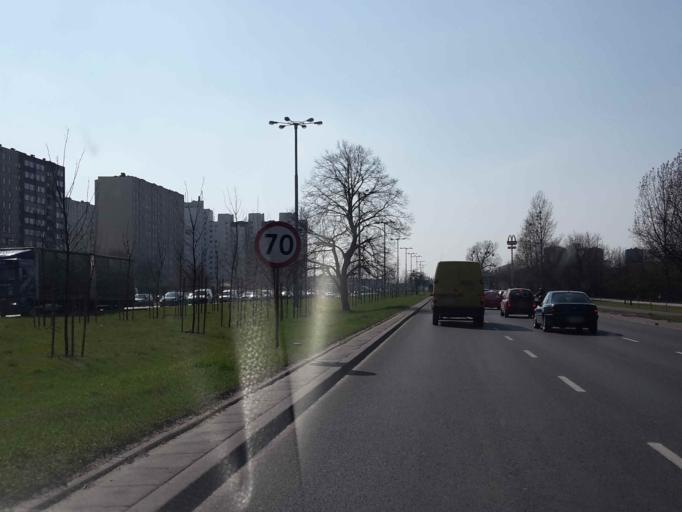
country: PL
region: Kujawsko-Pomorskie
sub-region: Powiat torunski
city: Lubicz Dolny
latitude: 53.0267
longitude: 18.6790
